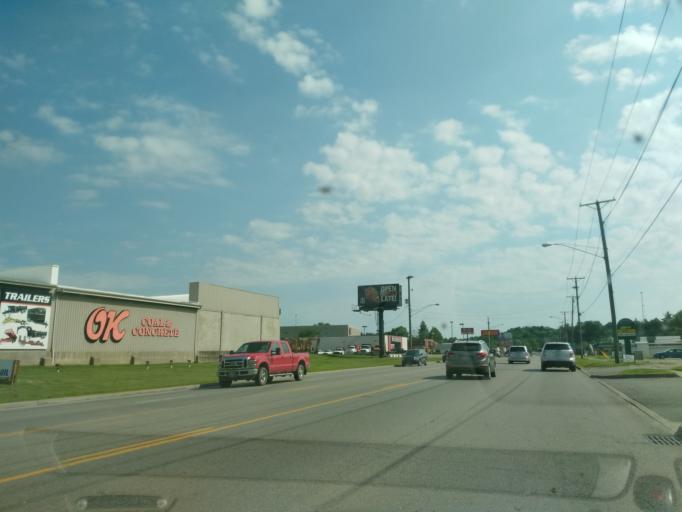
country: US
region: Ohio
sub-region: Muskingum County
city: South Zanesville
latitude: 39.9062
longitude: -82.0187
